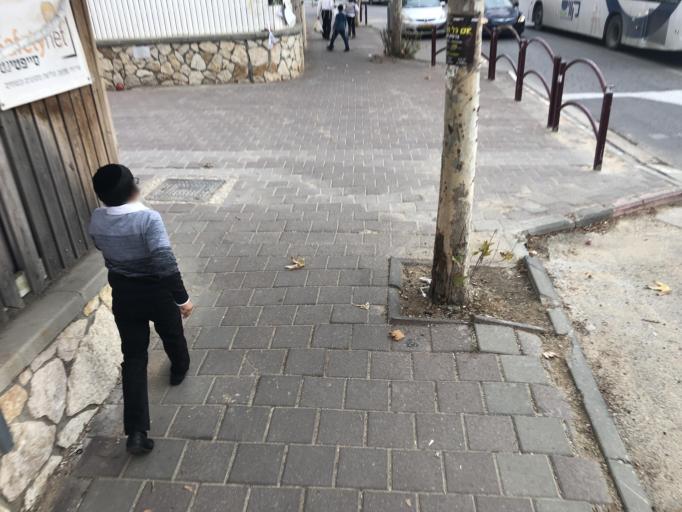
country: IL
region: Jerusalem
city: Modiin Ilit
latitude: 31.9387
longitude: 35.0431
